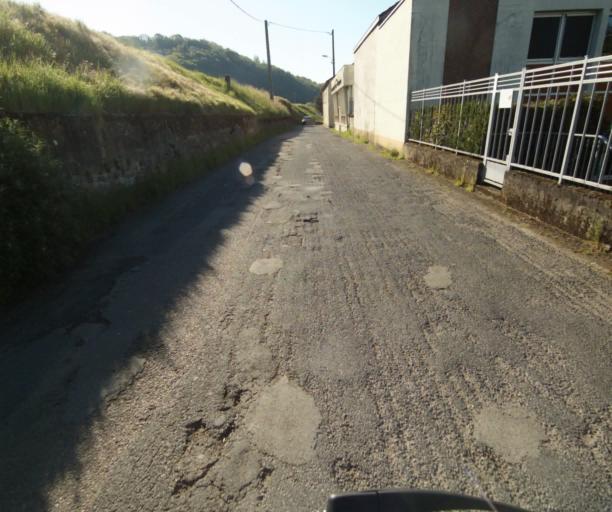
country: FR
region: Limousin
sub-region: Departement de la Correze
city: Tulle
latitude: 45.2582
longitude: 1.7561
